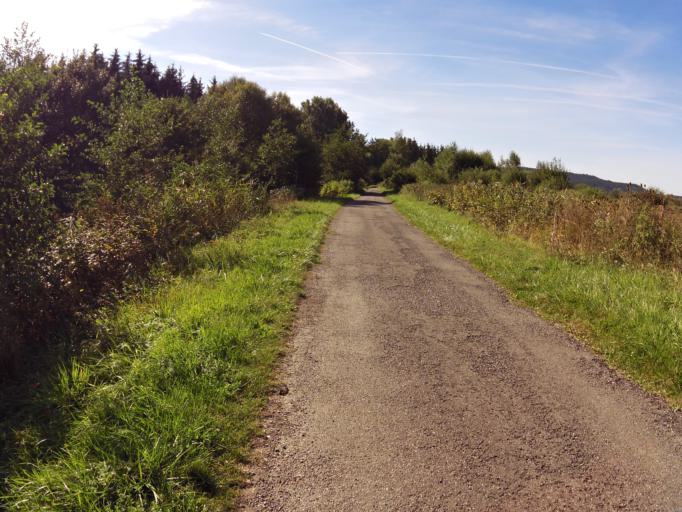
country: DE
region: Baden-Wuerttemberg
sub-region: Freiburg Region
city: Dauchingen
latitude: 48.0710
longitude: 8.5788
